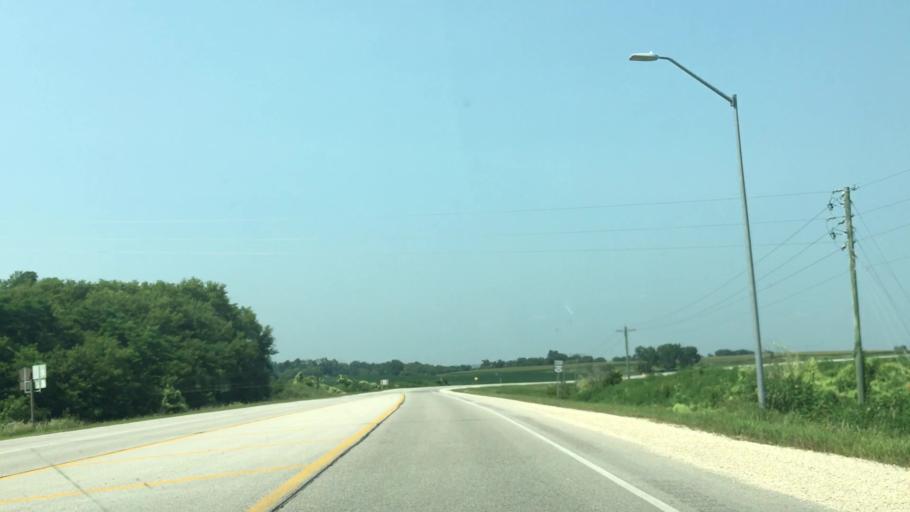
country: US
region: Iowa
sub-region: Winneshiek County
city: Decorah
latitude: 43.2056
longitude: -91.8782
